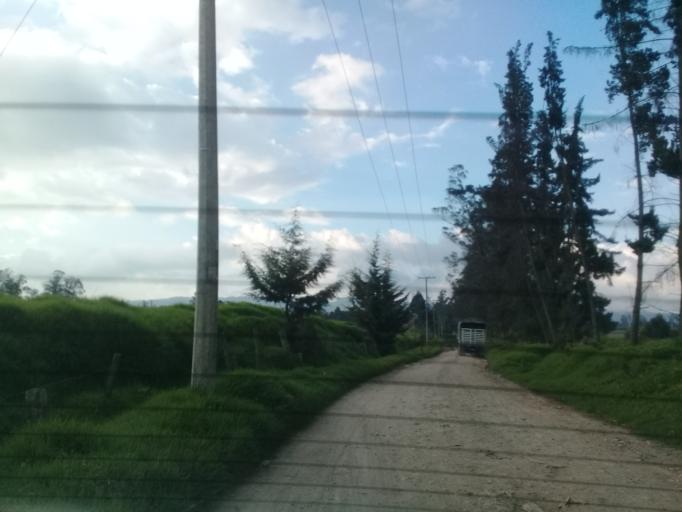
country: CO
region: Cundinamarca
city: Madrid
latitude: 4.7869
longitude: -74.2741
